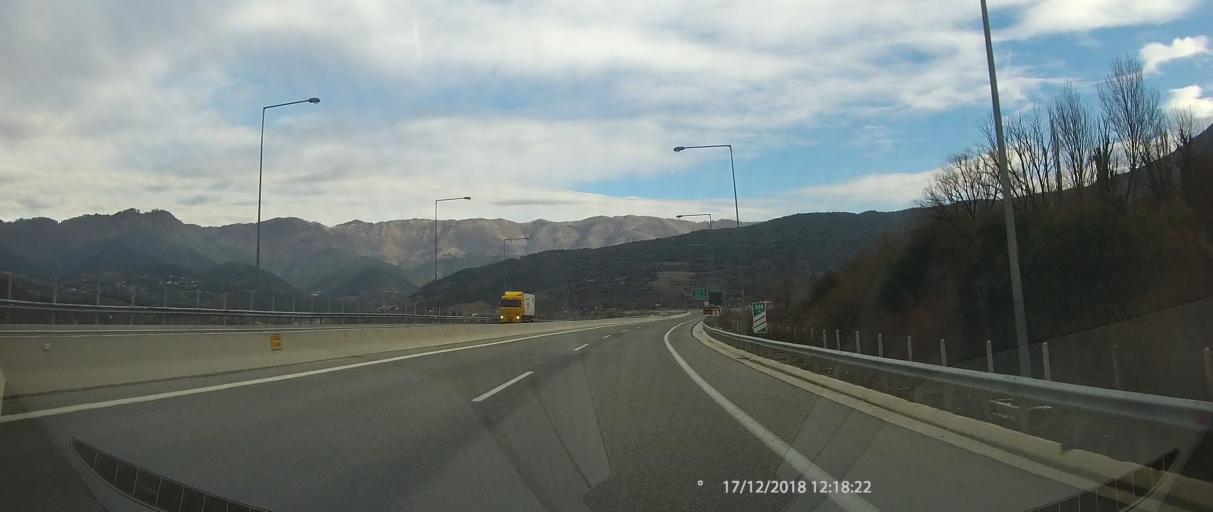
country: GR
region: Epirus
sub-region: Nomos Ioanninon
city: Metsovo
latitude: 39.7526
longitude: 21.0823
